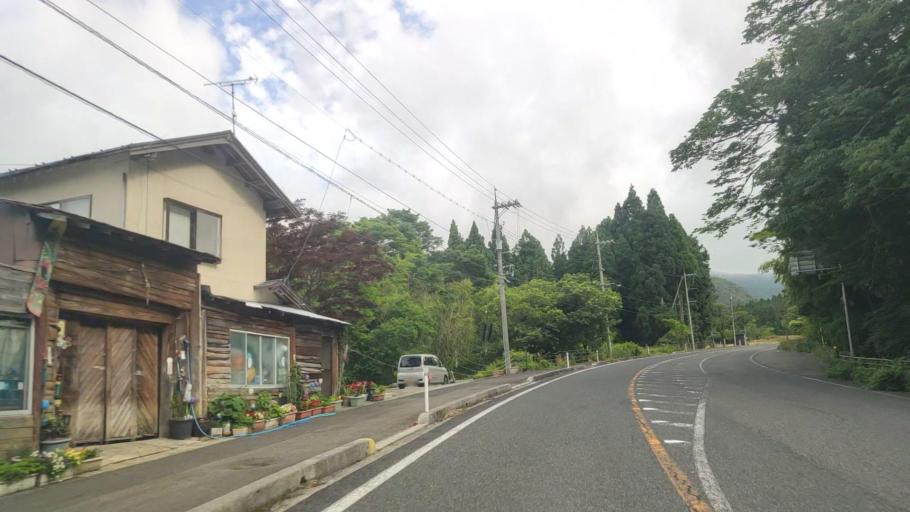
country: JP
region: Tottori
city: Yonago
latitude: 35.3242
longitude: 133.5566
